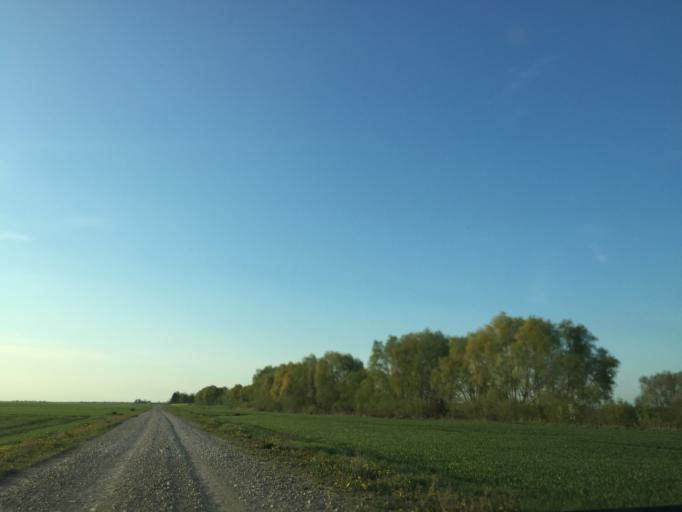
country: LV
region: Bauskas Rajons
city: Bauska
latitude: 56.2955
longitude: 24.1811
